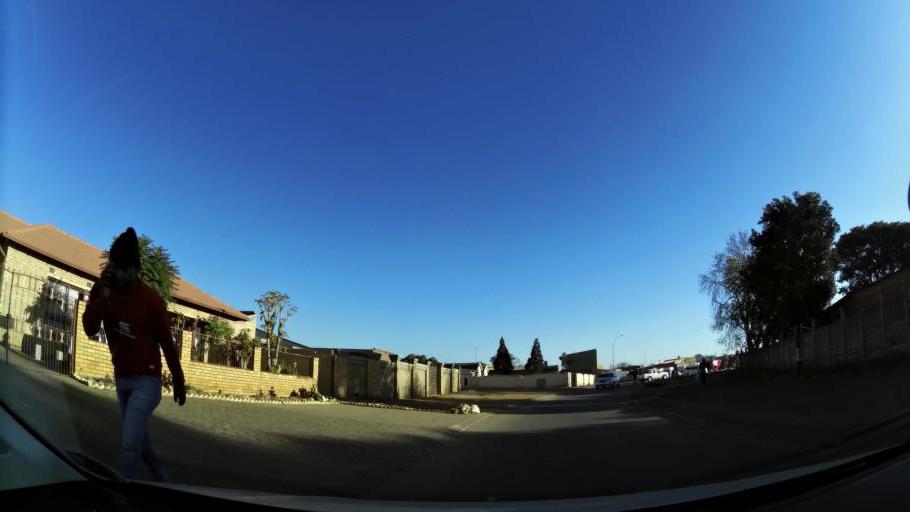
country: ZA
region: Gauteng
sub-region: Ekurhuleni Metropolitan Municipality
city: Tembisa
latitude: -26.0089
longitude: 28.2417
